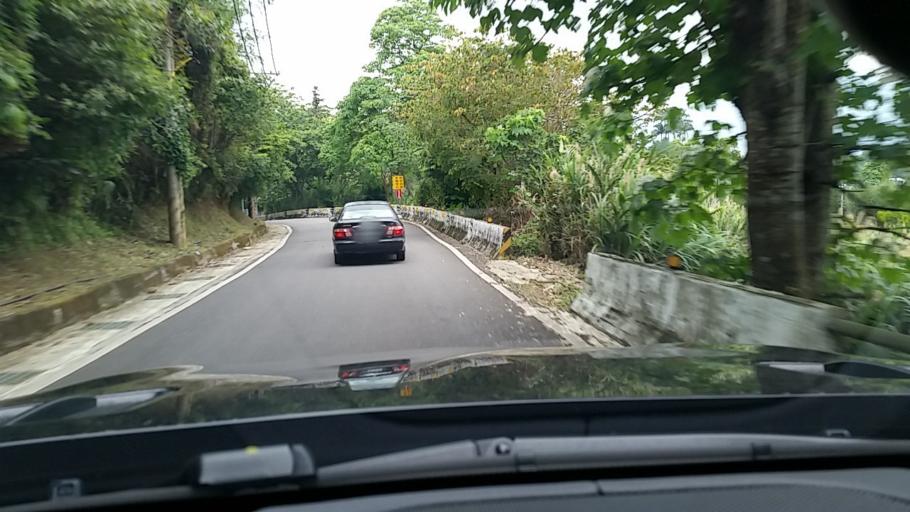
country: TW
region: Taiwan
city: Daxi
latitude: 24.7989
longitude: 121.3115
